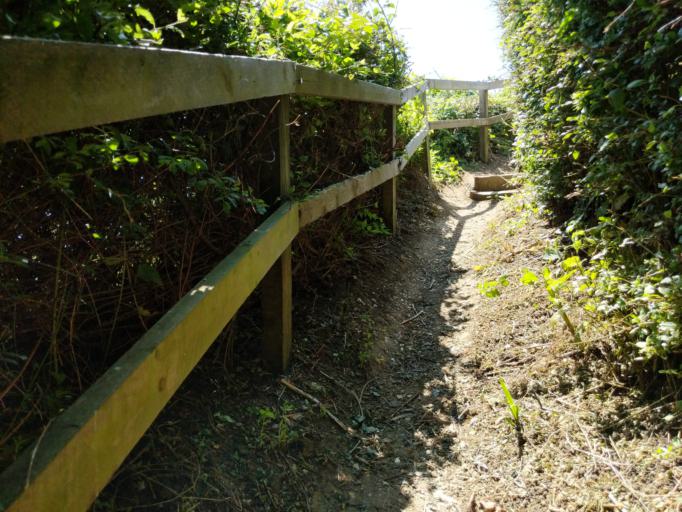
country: GB
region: England
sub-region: Kent
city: Folkestone
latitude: 51.1011
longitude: 1.2188
